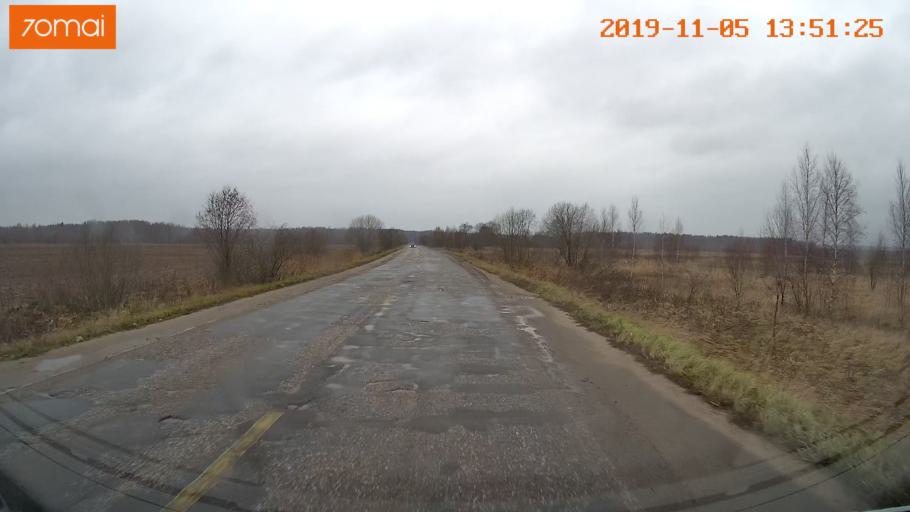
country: RU
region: Ivanovo
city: Kaminskiy
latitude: 57.0248
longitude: 41.4009
